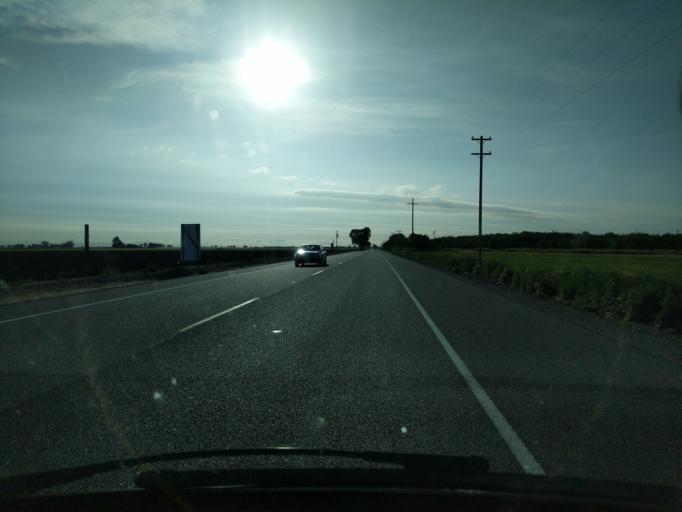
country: US
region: California
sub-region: San Joaquin County
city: Linden
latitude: 37.9364
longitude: -121.0907
